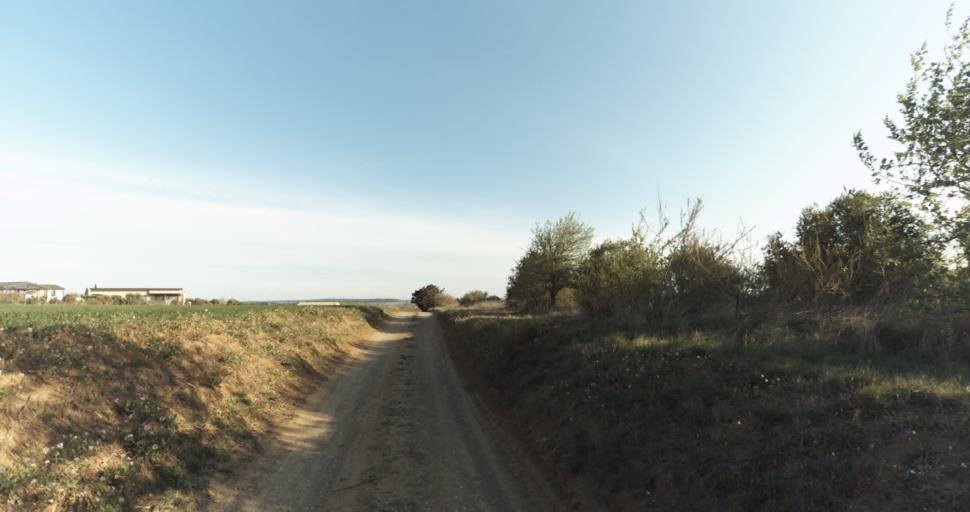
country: FR
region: Languedoc-Roussillon
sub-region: Departement de l'Herault
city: Pomerols
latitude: 43.3848
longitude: 3.5208
